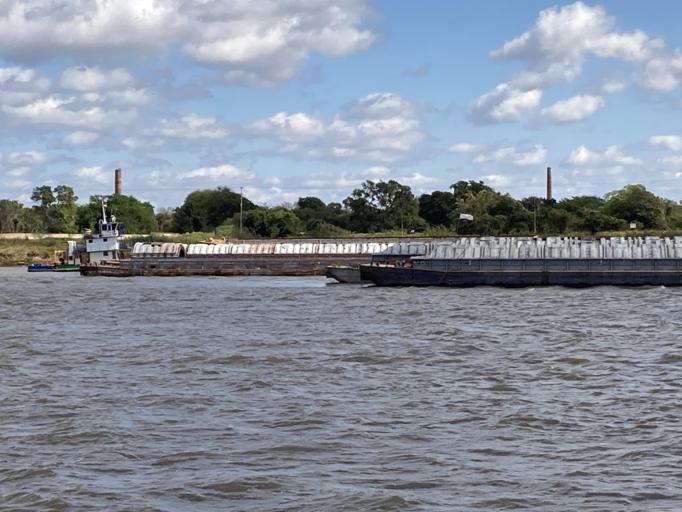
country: PY
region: Presidente Hayes
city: Nanawa
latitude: -25.2666
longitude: -57.6475
